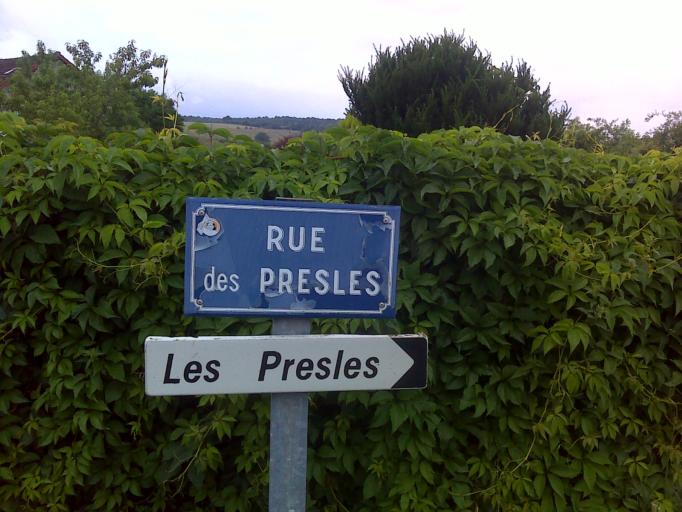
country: FR
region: Bourgogne
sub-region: Departement de Saone-et-Loire
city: Palinges
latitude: 46.5669
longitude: 4.2155
